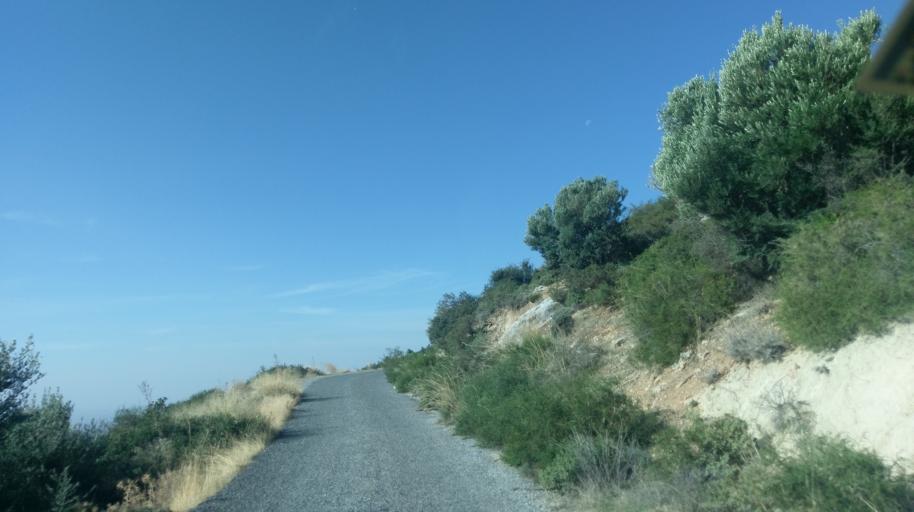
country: CY
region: Keryneia
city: Kyrenia
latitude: 35.2832
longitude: 33.4138
